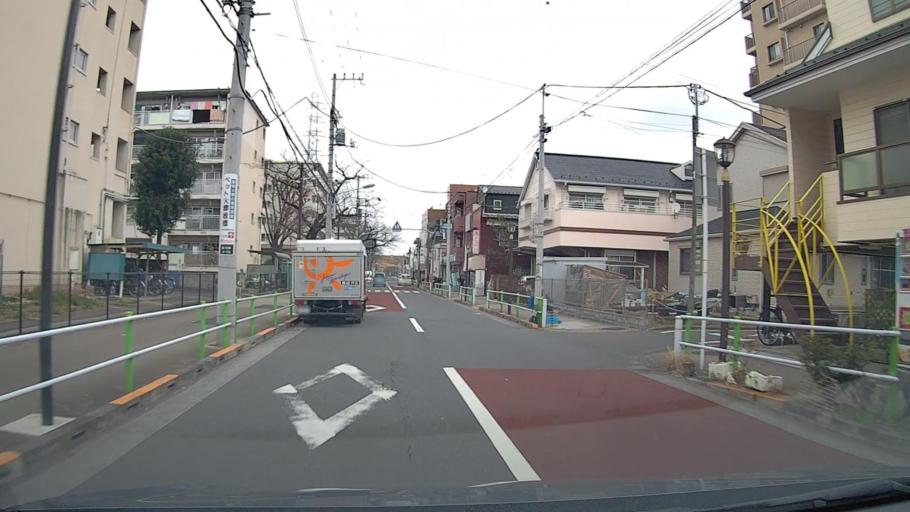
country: JP
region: Saitama
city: Shimotoda
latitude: 35.7952
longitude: 139.6641
